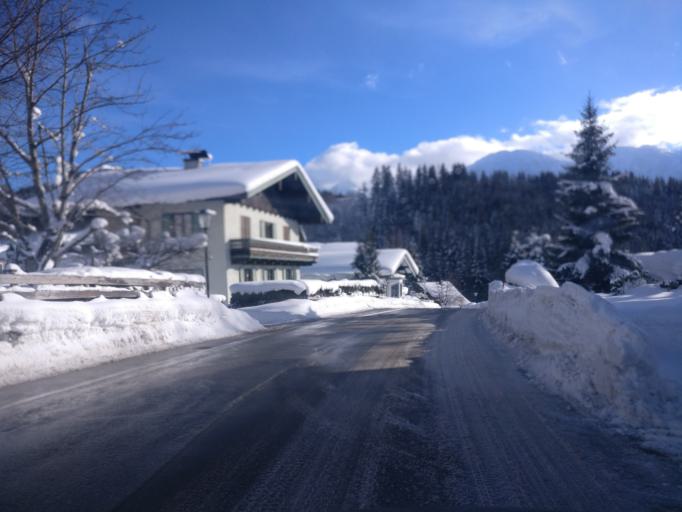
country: AT
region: Salzburg
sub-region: Politischer Bezirk Sankt Johann im Pongau
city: Goldegg
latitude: 47.3285
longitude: 13.0810
